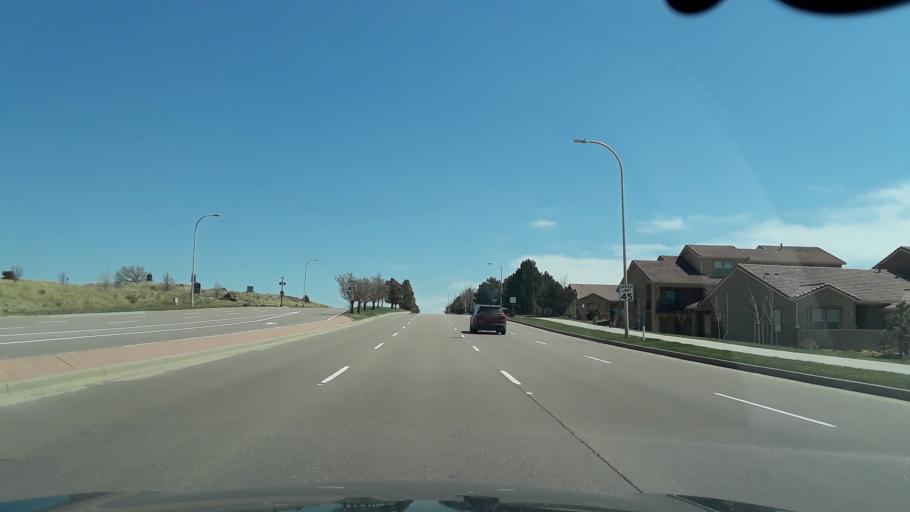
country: US
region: Colorado
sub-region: El Paso County
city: Black Forest
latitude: 38.9545
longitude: -104.7384
